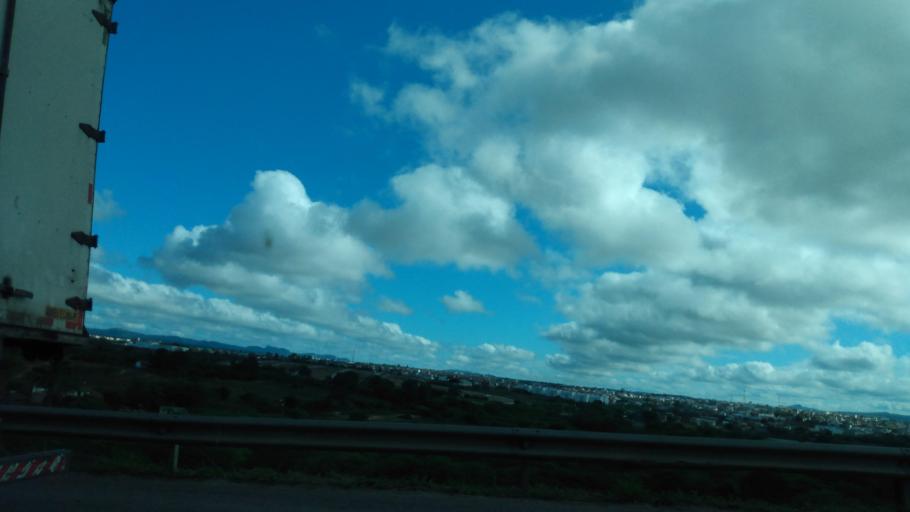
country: BR
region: Pernambuco
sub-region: Caruaru
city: Caruaru
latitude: -8.2998
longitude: -35.9931
